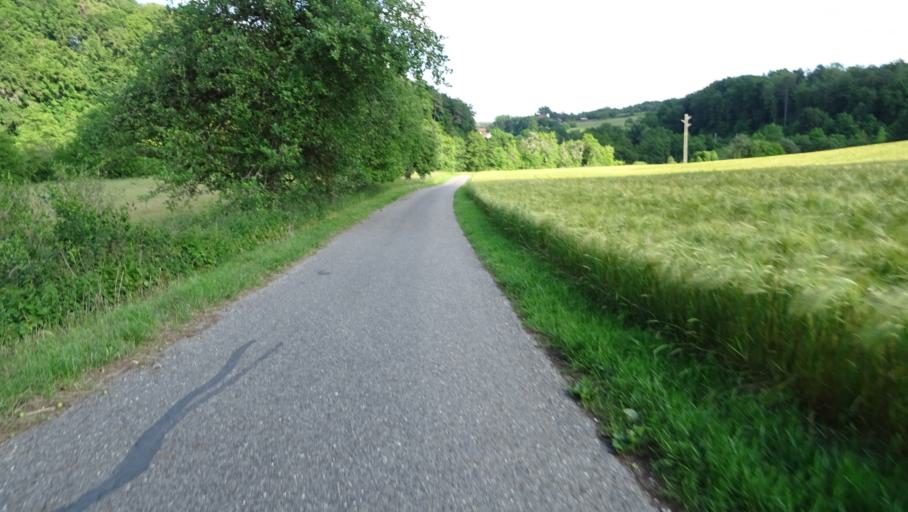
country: DE
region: Baden-Wuerttemberg
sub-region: Karlsruhe Region
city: Seckach
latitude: 49.4367
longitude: 9.3590
